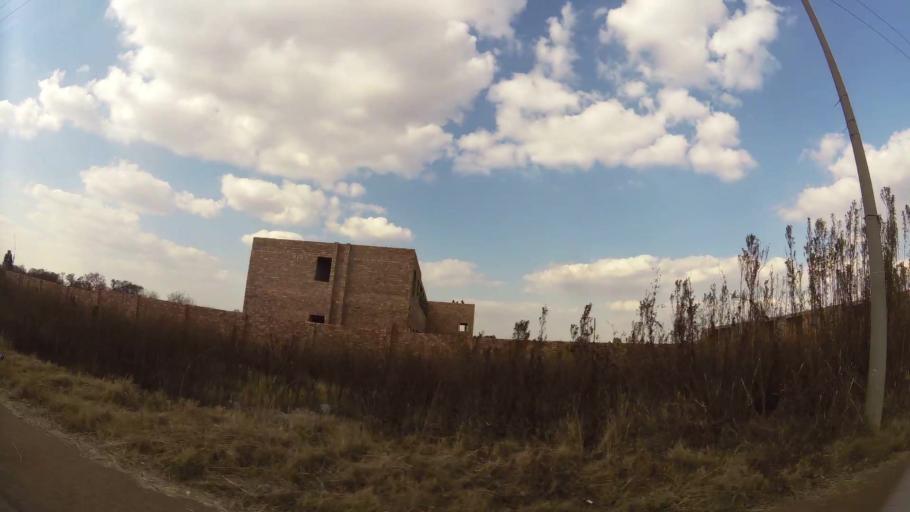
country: ZA
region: Mpumalanga
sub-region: Nkangala District Municipality
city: Delmas
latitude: -26.1454
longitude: 28.6760
